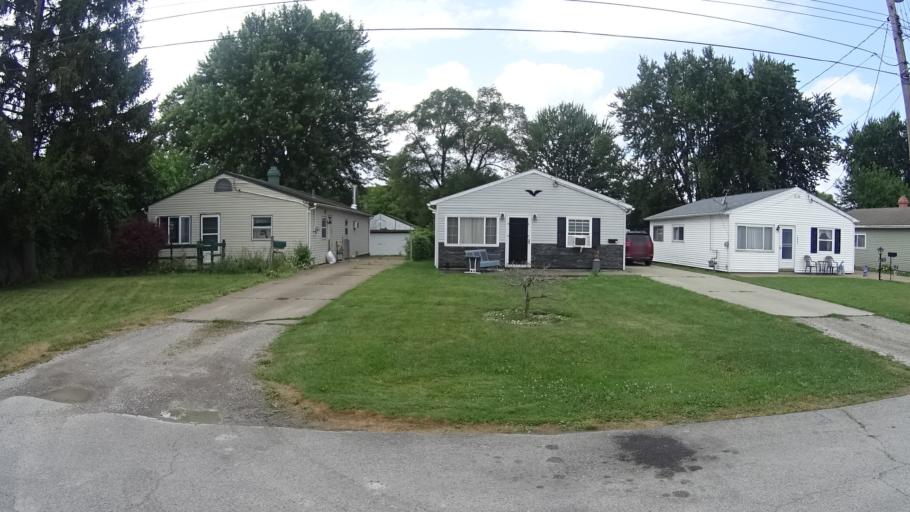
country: US
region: Ohio
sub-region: Erie County
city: Sandusky
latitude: 41.4450
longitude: -82.7437
